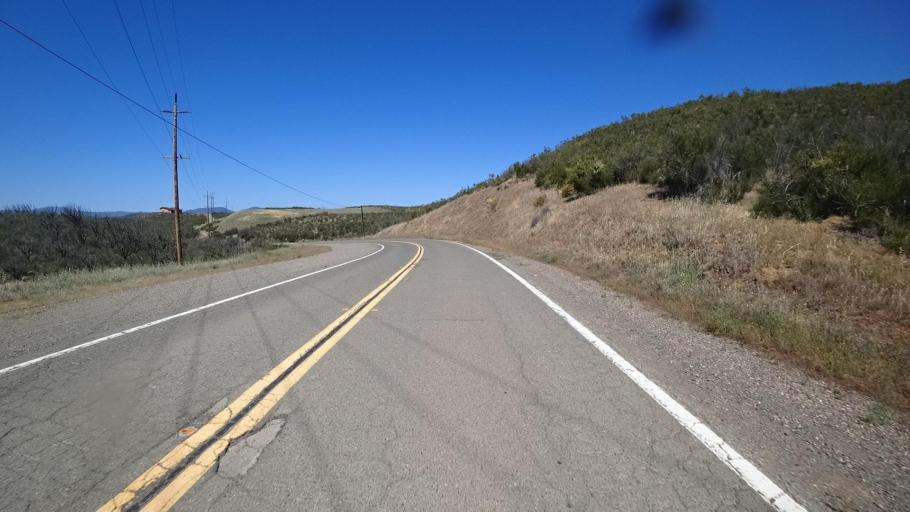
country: US
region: California
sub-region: Lake County
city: Hidden Valley Lake
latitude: 38.8847
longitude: -122.5163
